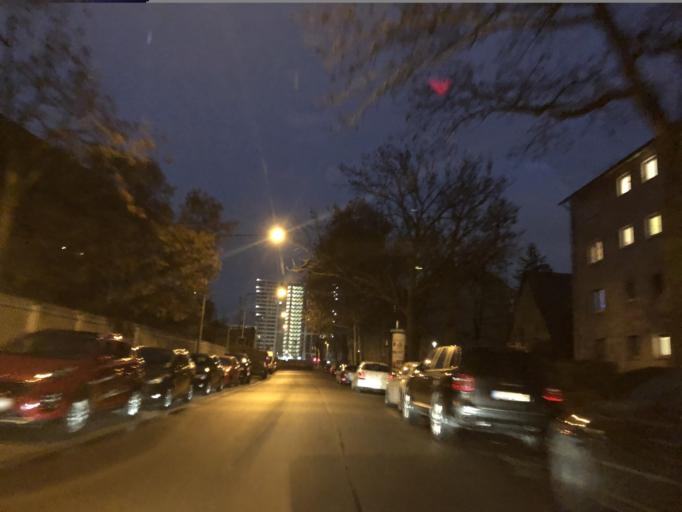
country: DE
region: Hesse
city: Niederrad
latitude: 50.1122
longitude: 8.6354
